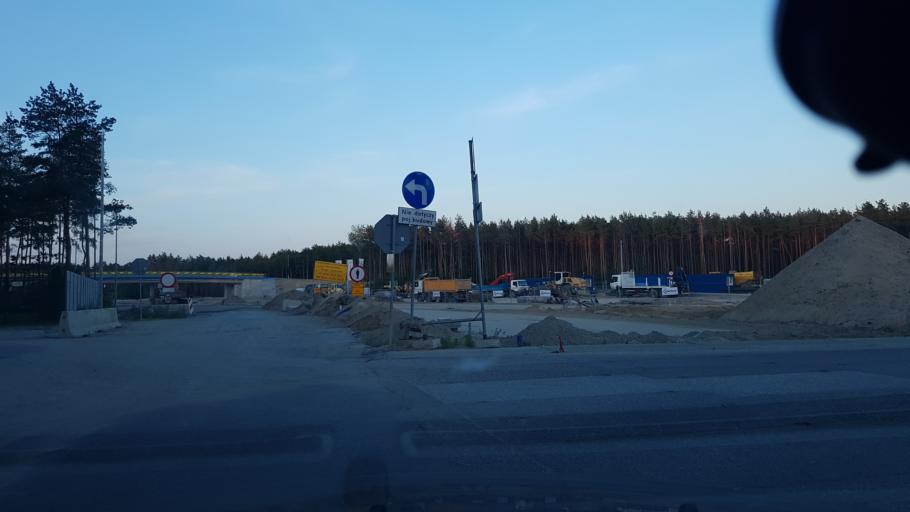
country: PL
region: Masovian Voivodeship
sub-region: Warszawa
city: Wawer
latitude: 52.1704
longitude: 21.2079
